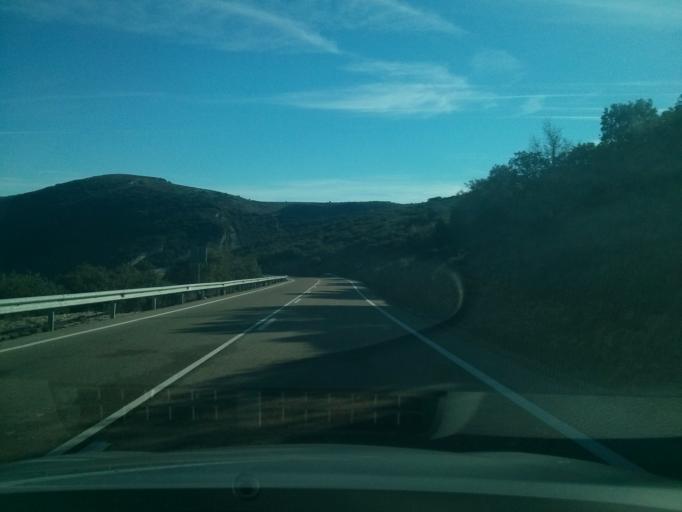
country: ES
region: Castille and Leon
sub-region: Provincia de Burgos
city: Rucandio
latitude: 42.8313
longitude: -3.6152
